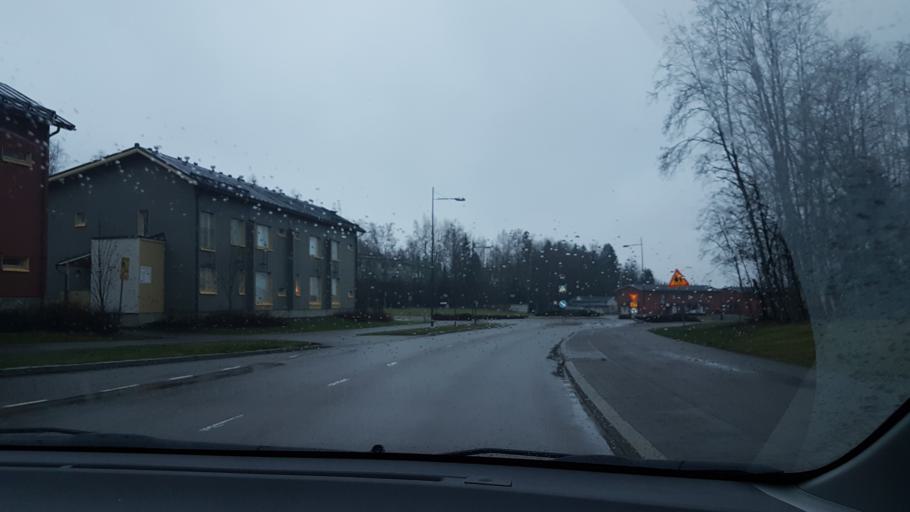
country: FI
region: Uusimaa
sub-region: Helsinki
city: Espoo
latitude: 60.1929
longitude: 24.5928
